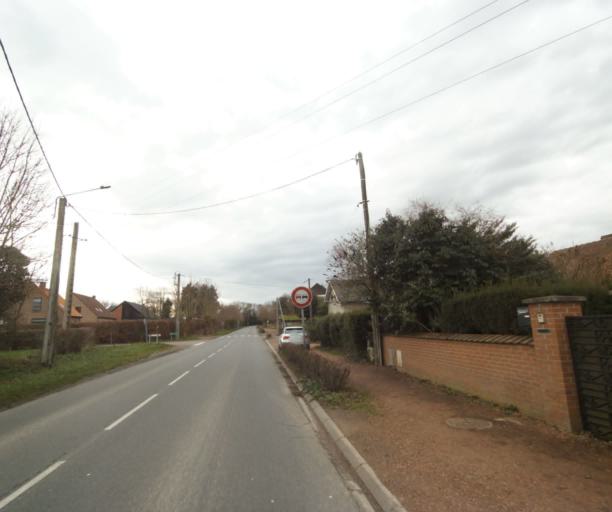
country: FR
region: Nord-Pas-de-Calais
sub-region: Departement du Nord
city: Sebourg
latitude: 50.3428
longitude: 3.6397
